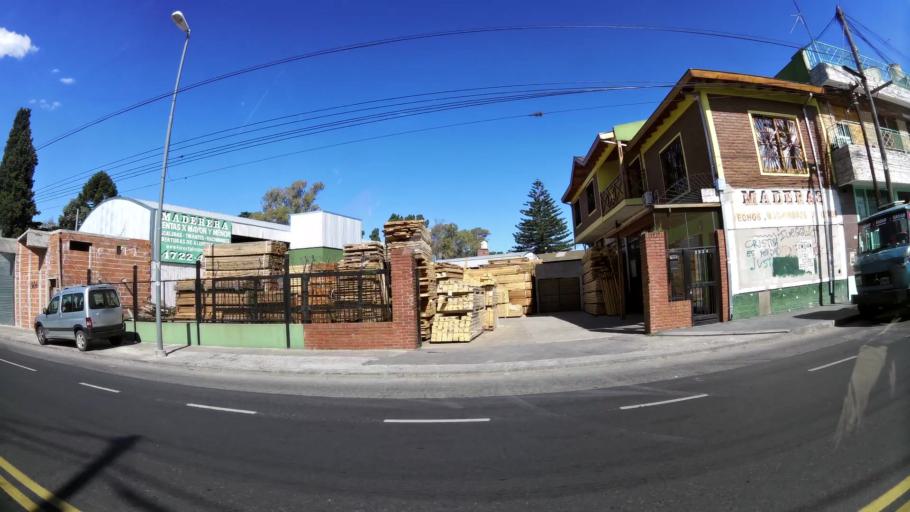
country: AR
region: Buenos Aires
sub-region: Partido de General San Martin
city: General San Martin
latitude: -34.5258
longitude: -58.5725
